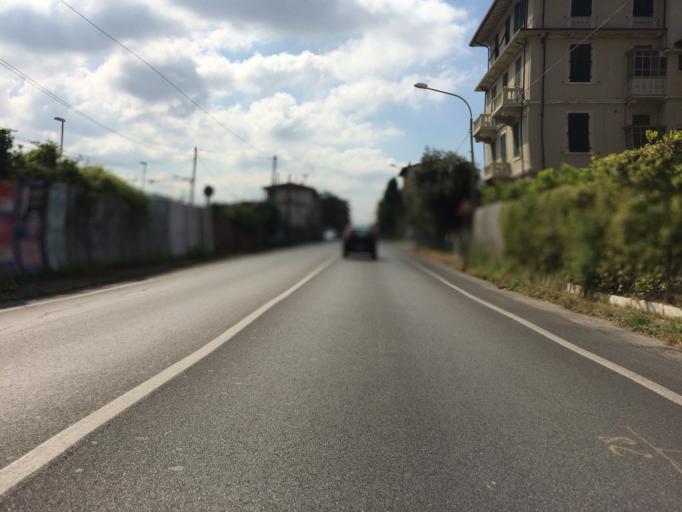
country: IT
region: Tuscany
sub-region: Provincia di Lucca
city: Ripa-Pozzi-Querceta-Ponterosso
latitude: 43.9787
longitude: 10.1977
